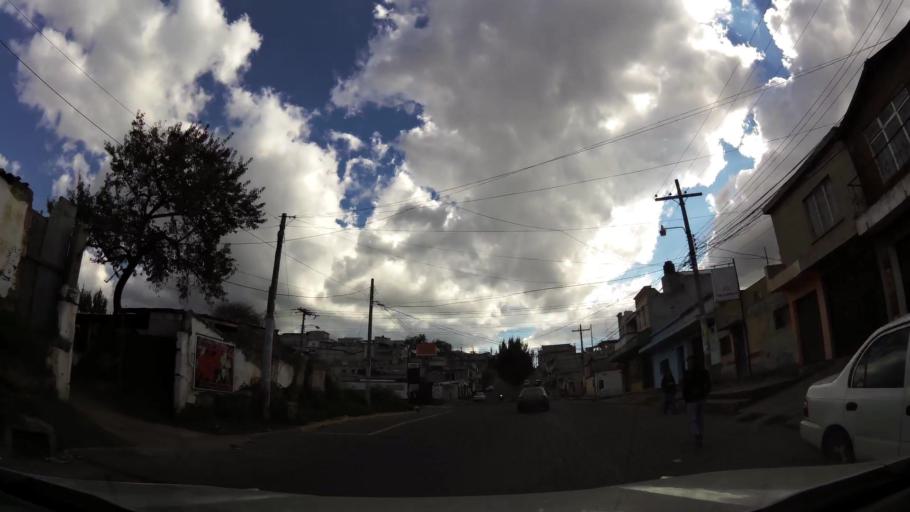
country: GT
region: Quetzaltenango
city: Quetzaltenango
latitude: 14.8506
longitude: -91.5184
